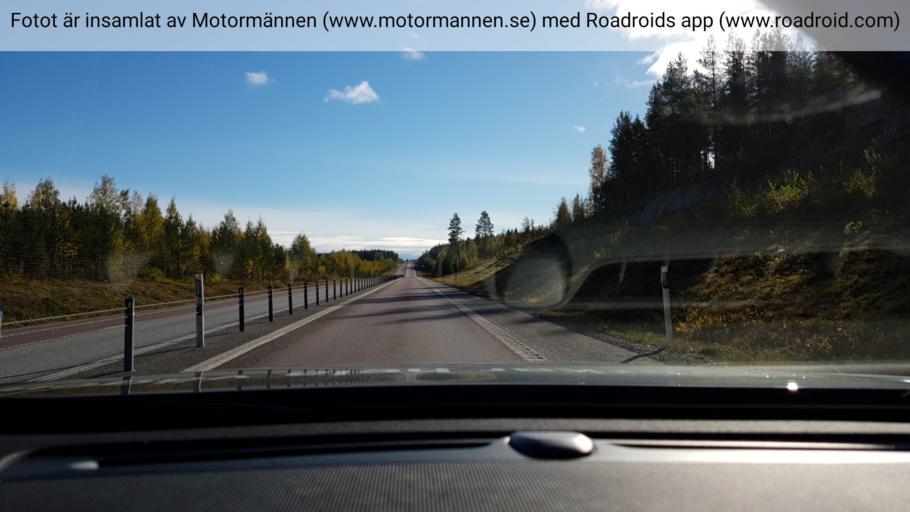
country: SE
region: Vaesterbotten
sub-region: Skelleftea Kommun
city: Soedra Bergsbyn
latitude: 64.6944
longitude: 21.0232
